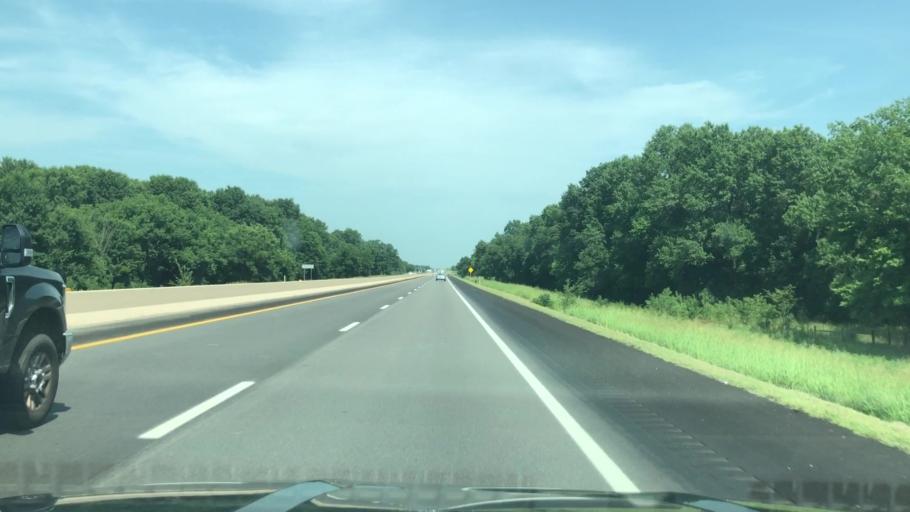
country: US
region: Oklahoma
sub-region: Craig County
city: Vinita
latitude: 36.6592
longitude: -95.0946
